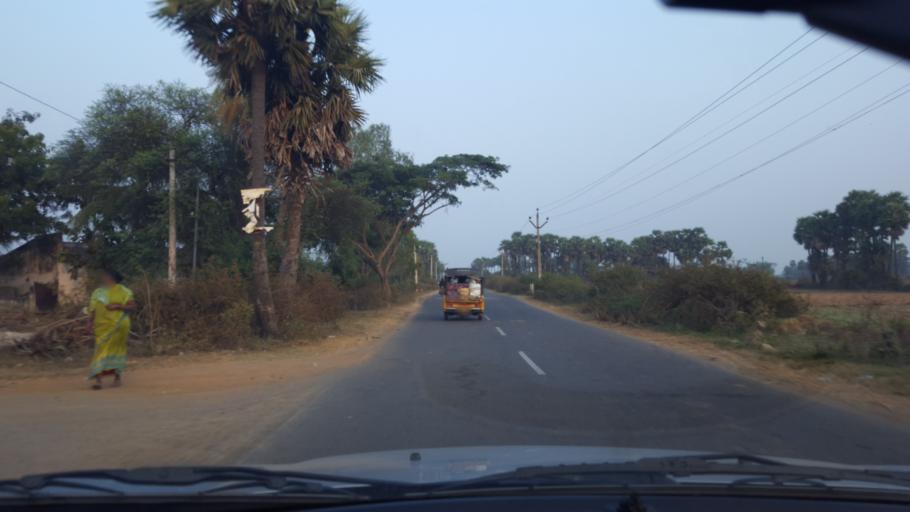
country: IN
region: Andhra Pradesh
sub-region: Srikakulam
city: Amudalavalasa
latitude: 18.3844
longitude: 83.9310
